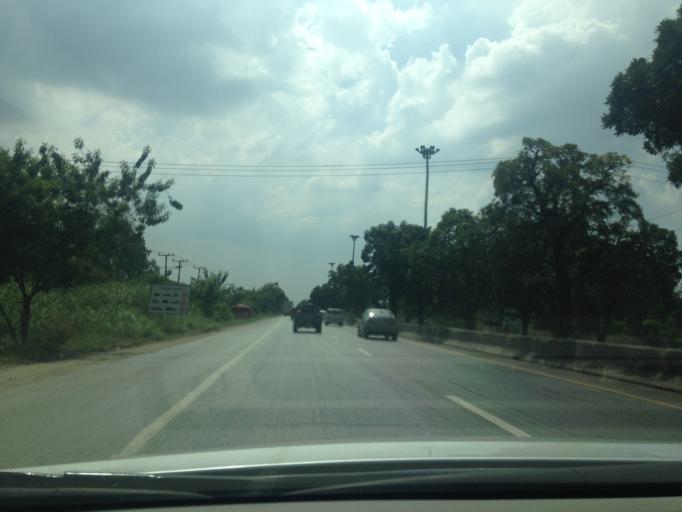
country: TH
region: Pathum Thani
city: Sam Khok
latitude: 14.0885
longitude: 100.5132
